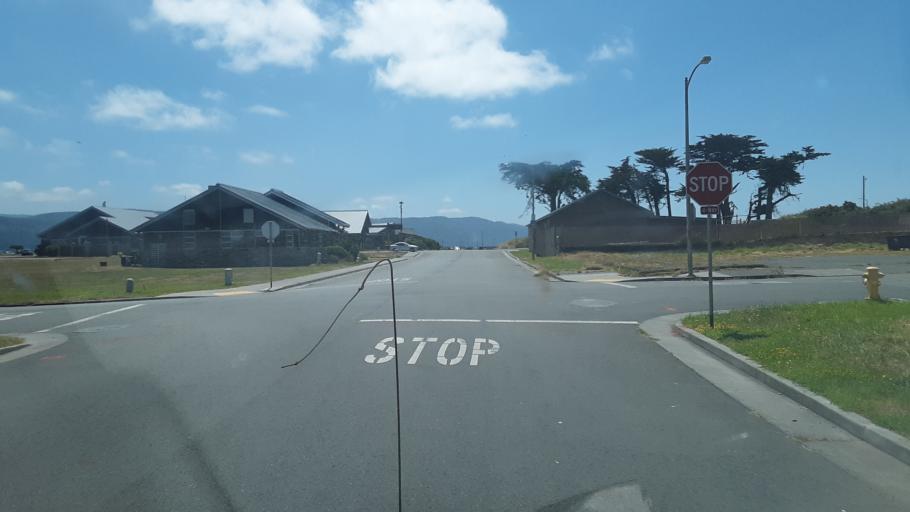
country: US
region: California
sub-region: Del Norte County
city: Crescent City
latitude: 41.7482
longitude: -124.2022
